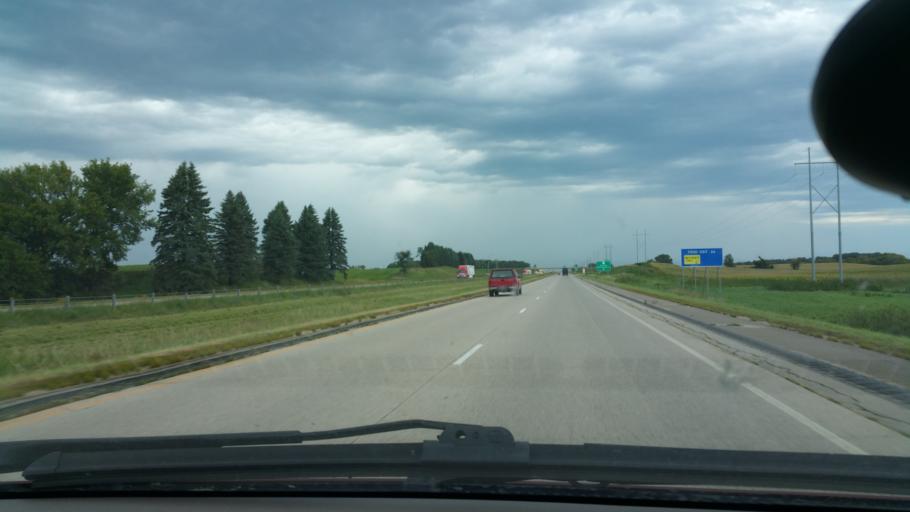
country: US
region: Minnesota
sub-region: Rice County
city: Dundas
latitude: 44.4205
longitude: -93.2924
